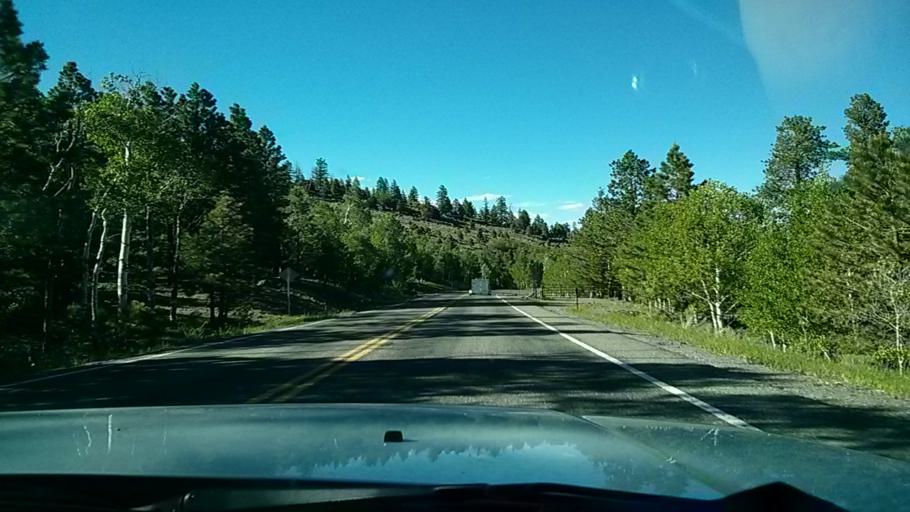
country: US
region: Utah
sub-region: Wayne County
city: Loa
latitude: 38.1279
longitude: -111.3287
